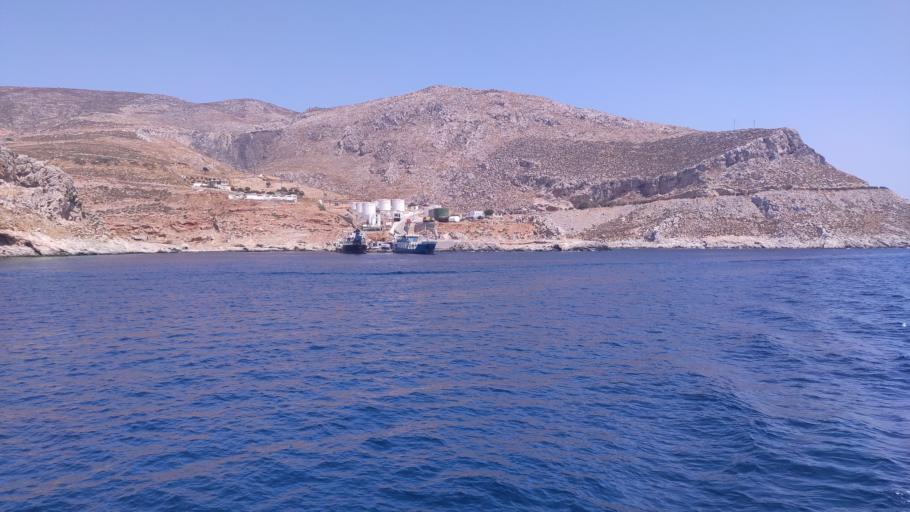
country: GR
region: South Aegean
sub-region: Nomos Dodekanisou
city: Kalymnos
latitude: 36.9465
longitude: 27.0096
